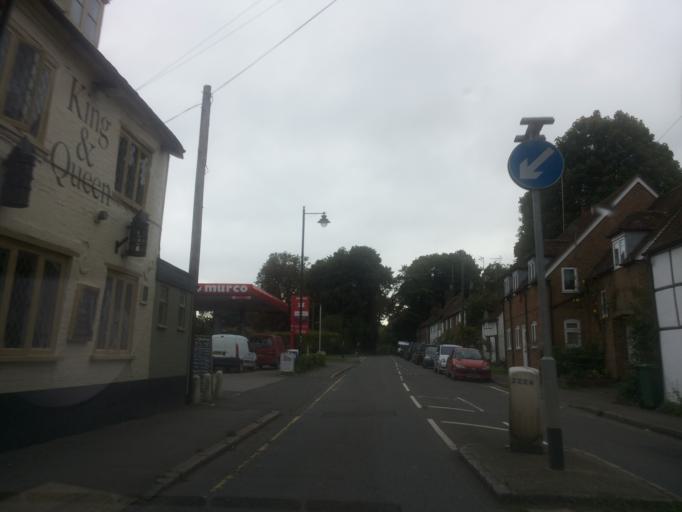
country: GB
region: England
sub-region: Buckinghamshire
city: Wendover
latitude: 51.7608
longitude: -0.7438
